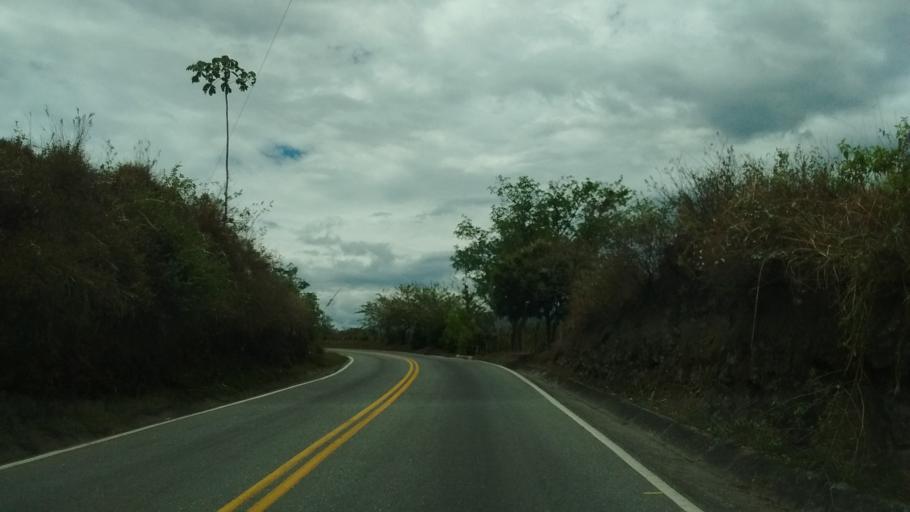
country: CO
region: Cauca
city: La Sierra
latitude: 2.2126
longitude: -76.7978
